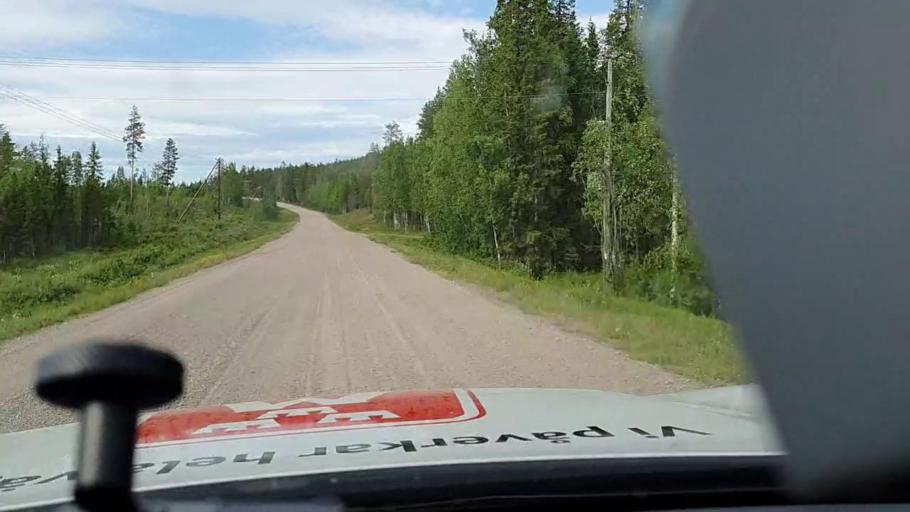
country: SE
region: Norrbotten
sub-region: Alvsbyns Kommun
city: AElvsbyn
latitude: 66.1270
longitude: 20.9969
